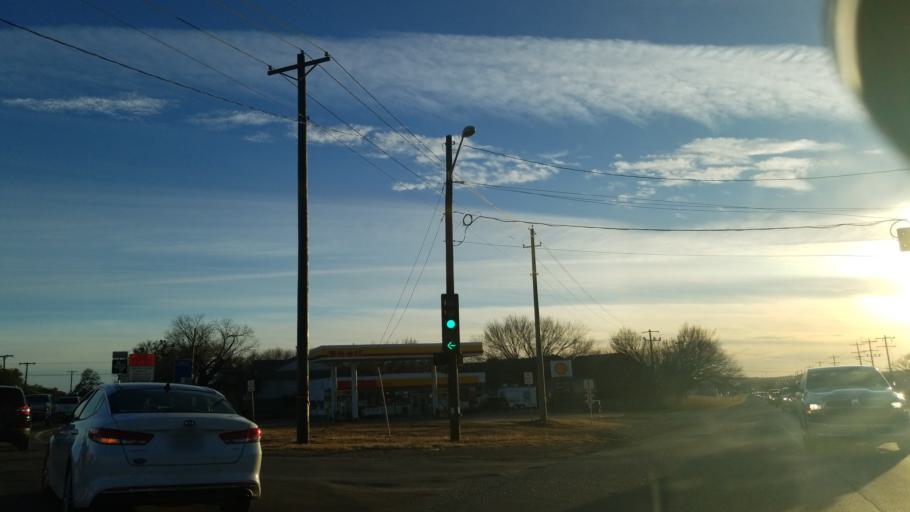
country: US
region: Texas
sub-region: Denton County
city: Denton
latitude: 33.1771
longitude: -97.1420
